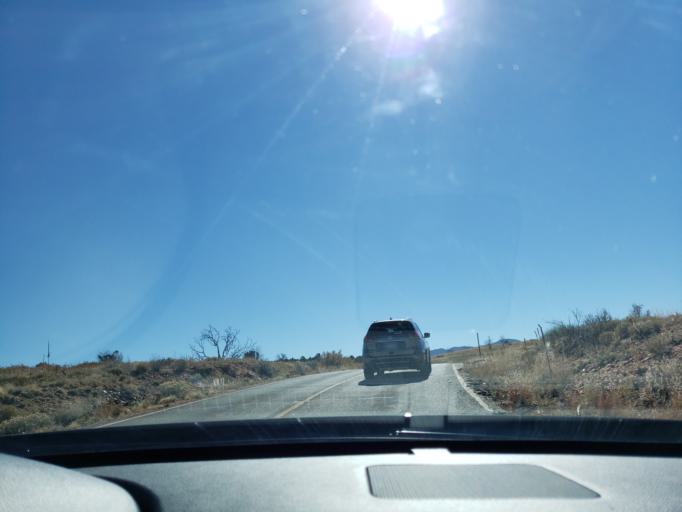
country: US
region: Colorado
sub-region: Fremont County
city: Canon City
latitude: 38.4695
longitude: -105.3071
